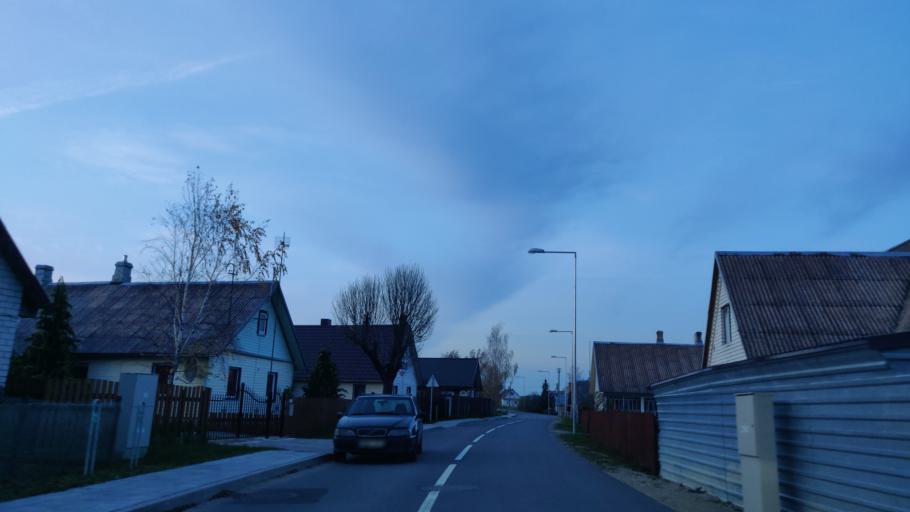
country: LT
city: Lentvaris
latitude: 54.5869
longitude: 25.0511
